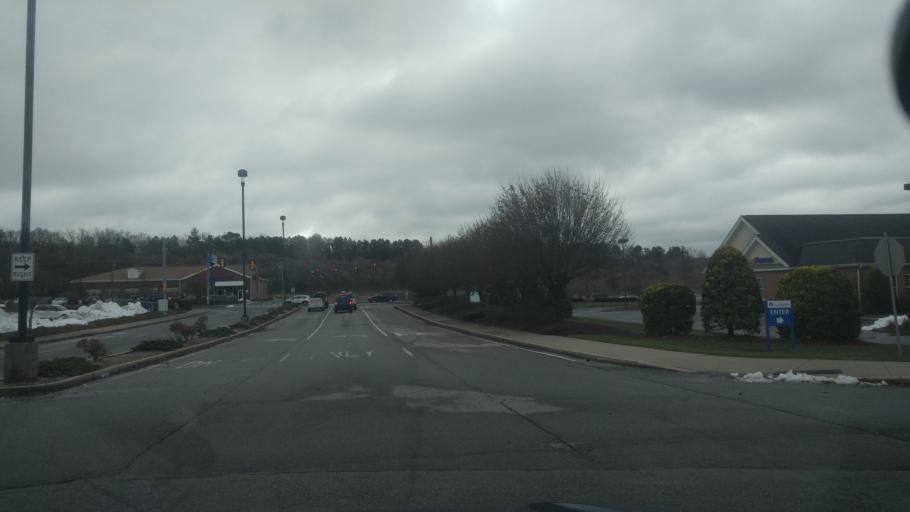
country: US
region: Rhode Island
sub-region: Kent County
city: West Warwick
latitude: 41.6625
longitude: -71.5495
